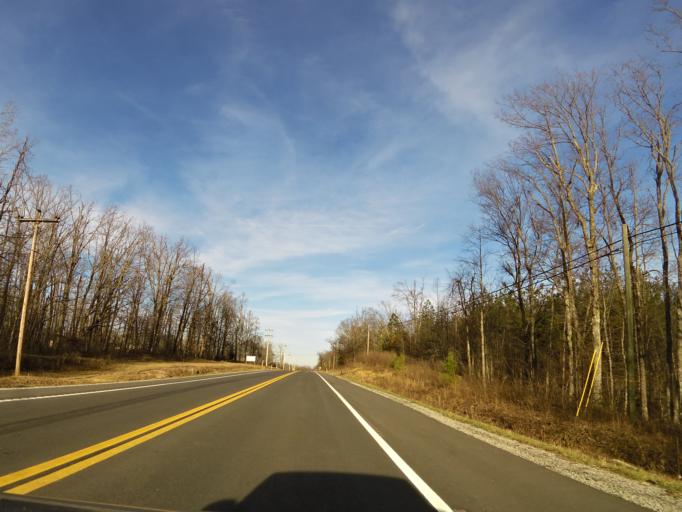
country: US
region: Tennessee
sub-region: White County
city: Sparta
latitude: 35.9616
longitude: -85.2825
